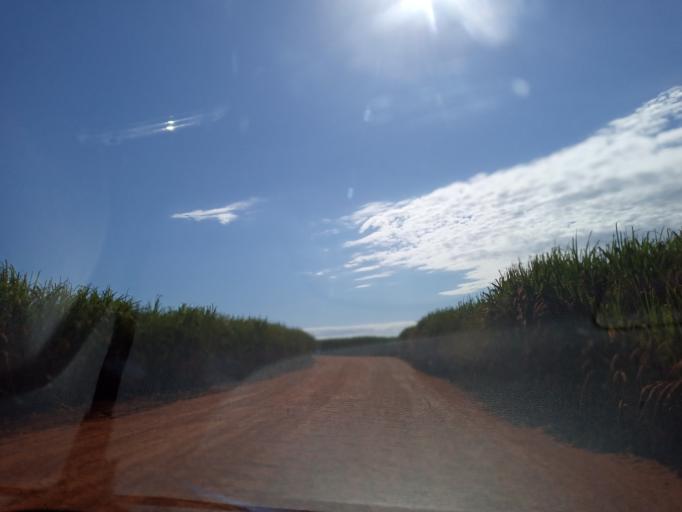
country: BR
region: Goias
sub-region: Itumbiara
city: Itumbiara
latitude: -18.4499
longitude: -49.1798
